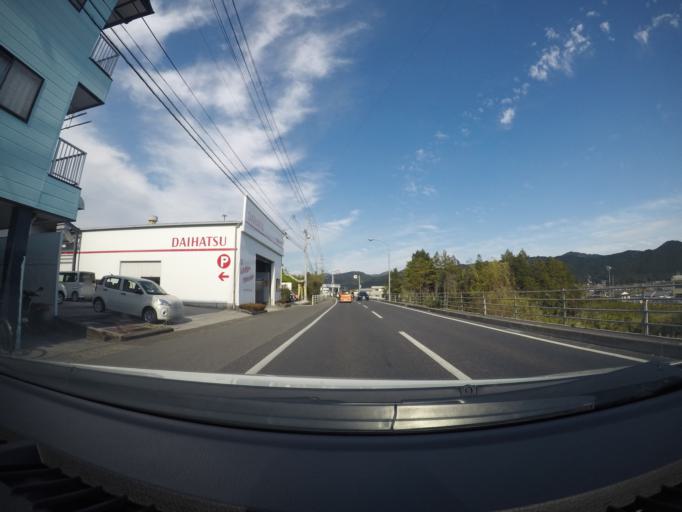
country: JP
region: Kochi
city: Kochi-shi
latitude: 33.6089
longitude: 133.7015
